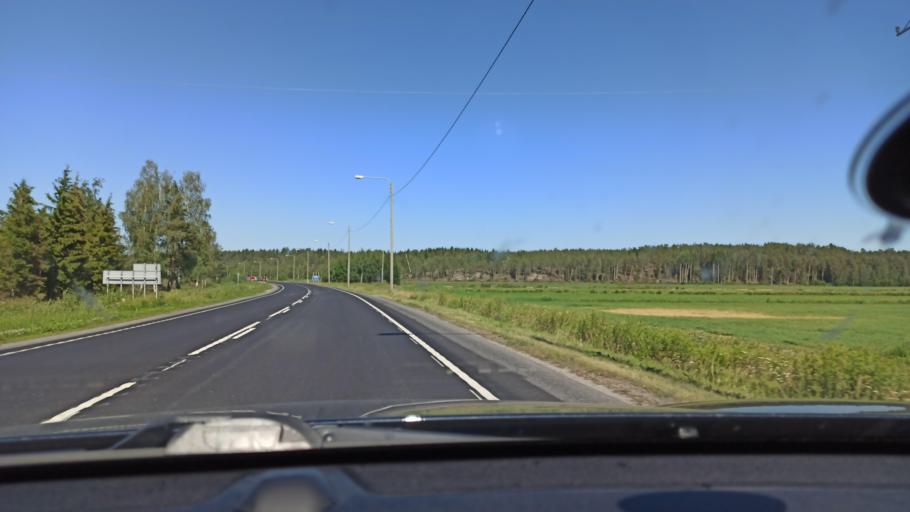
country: FI
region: Ostrobothnia
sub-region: Vaasa
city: Oravais
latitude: 63.2848
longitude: 22.3624
